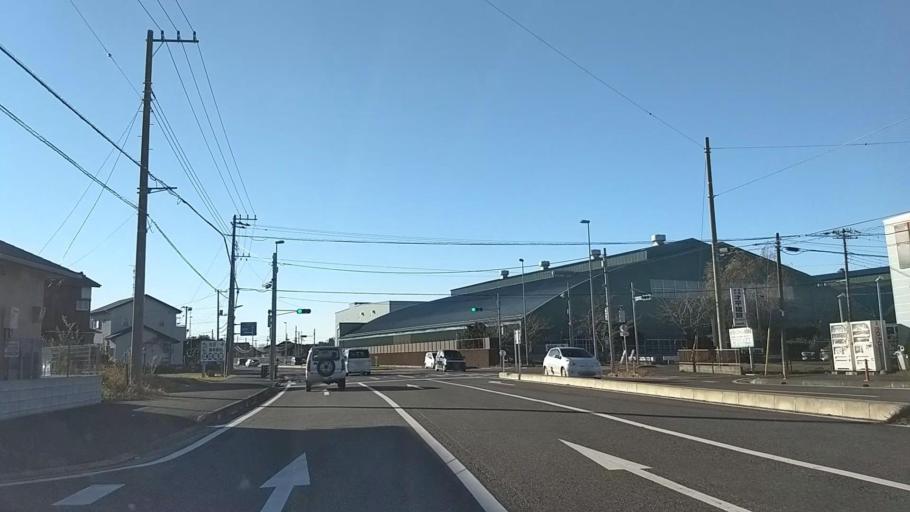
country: JP
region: Chiba
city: Kisarazu
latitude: 35.4061
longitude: 139.9185
